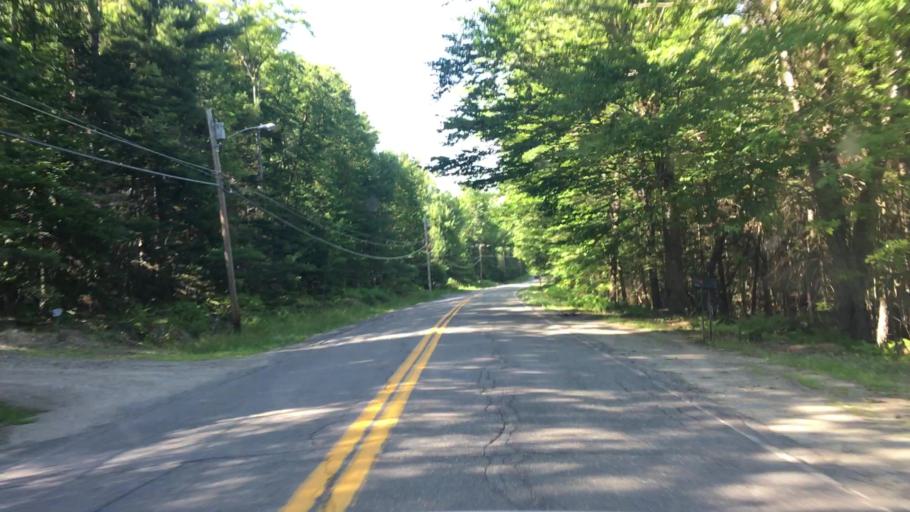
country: US
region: Maine
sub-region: Penobscot County
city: Enfield
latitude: 45.2686
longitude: -68.5617
